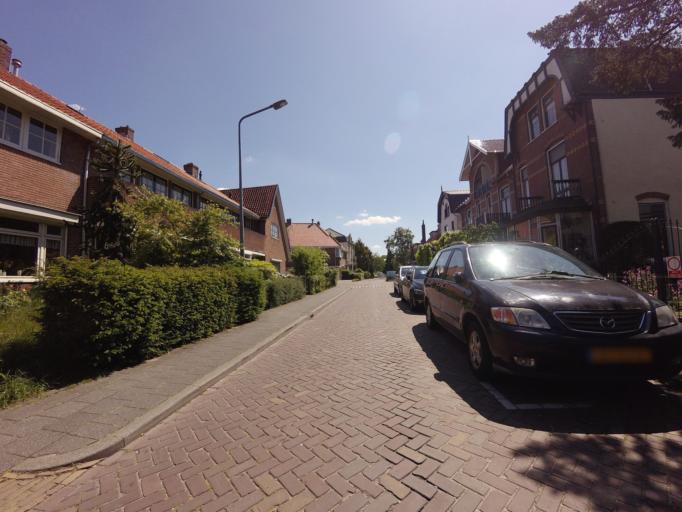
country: NL
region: North Holland
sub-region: Gemeente Hilversum
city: Hilversum
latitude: 52.2198
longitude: 5.1820
